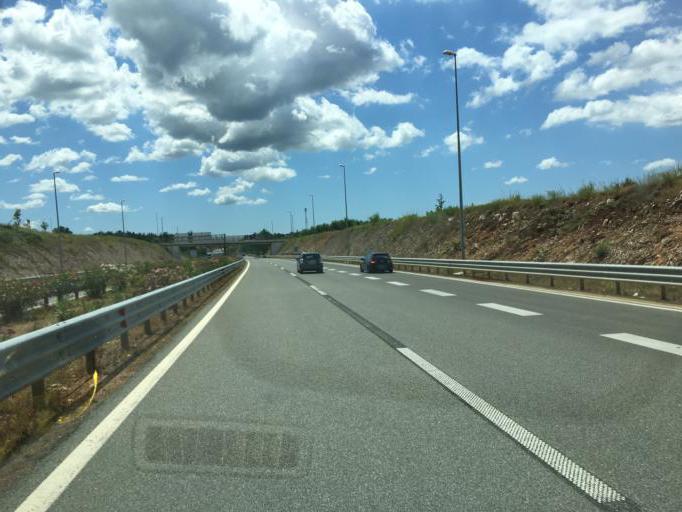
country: HR
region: Istarska
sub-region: Grad Porec
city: Porec
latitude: 45.2161
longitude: 13.7234
